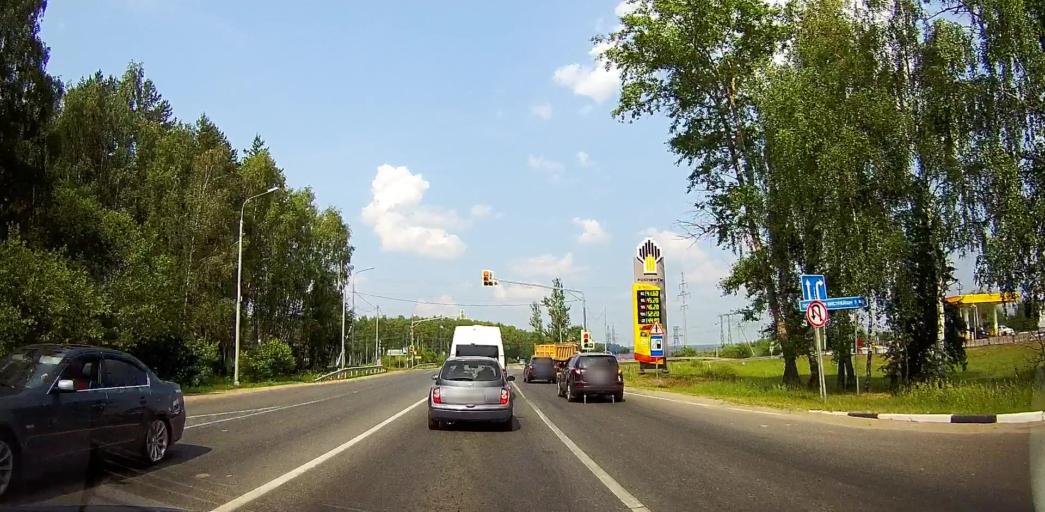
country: RU
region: Moskovskaya
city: Stupino
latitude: 54.9258
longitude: 38.1172
